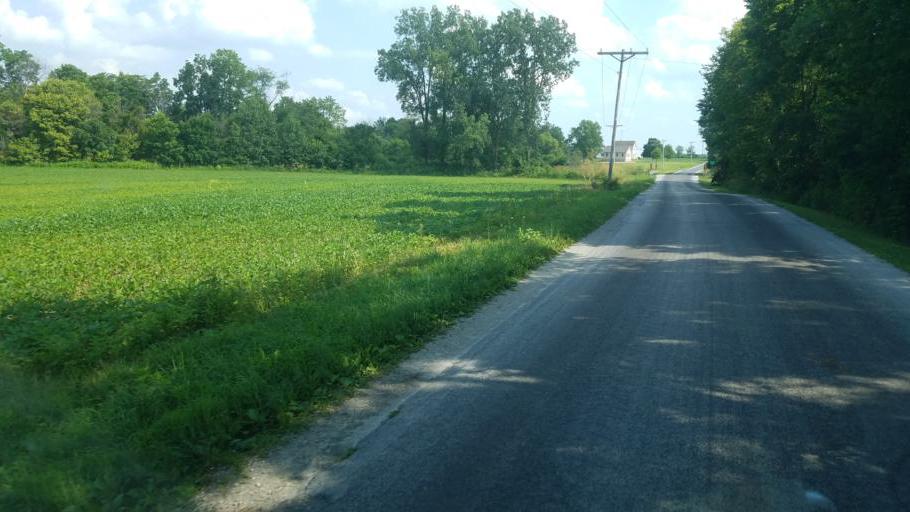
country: US
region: Ohio
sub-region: Hardin County
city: Kenton
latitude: 40.5799
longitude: -83.4544
